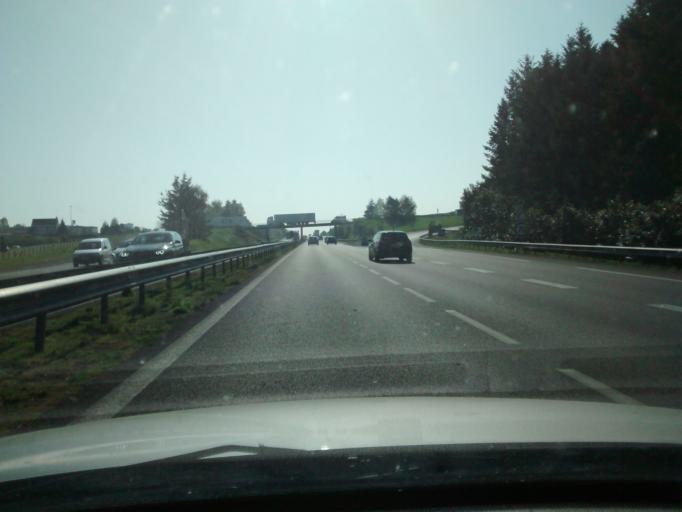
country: FR
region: Brittany
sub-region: Departement d'Ille-et-Vilaine
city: Noyal-sur-Vilaine
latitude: 48.1113
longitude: -1.5361
